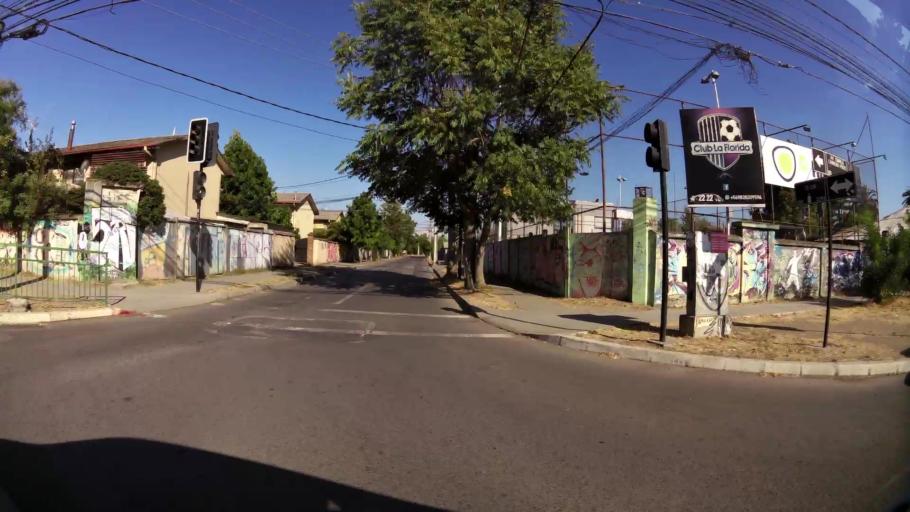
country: CL
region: Maule
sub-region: Provincia de Talca
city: Talca
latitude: -35.4339
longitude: -71.6789
